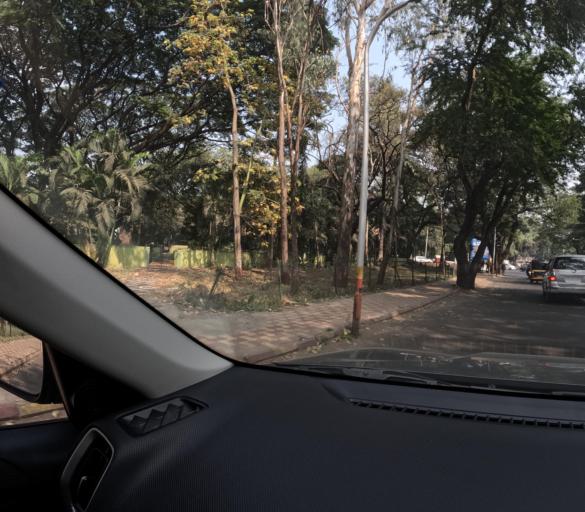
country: IN
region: Maharashtra
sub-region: Pune Division
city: Pune
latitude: 18.5233
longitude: 73.8871
